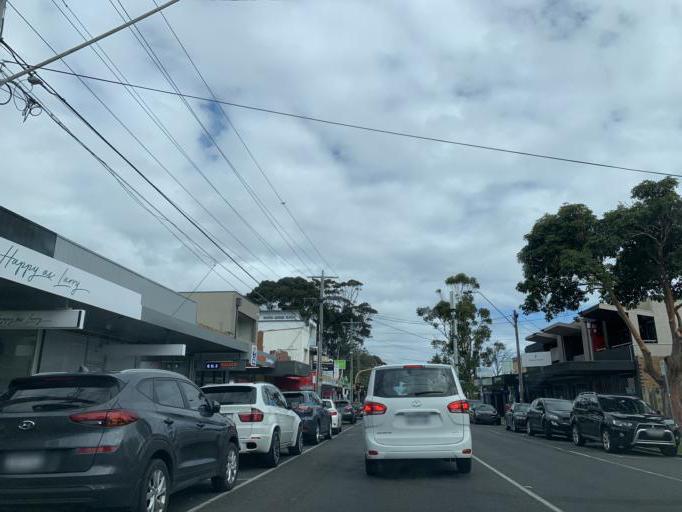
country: AU
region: Victoria
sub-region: Bayside
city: Cheltenham
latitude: -37.9790
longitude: 145.0532
